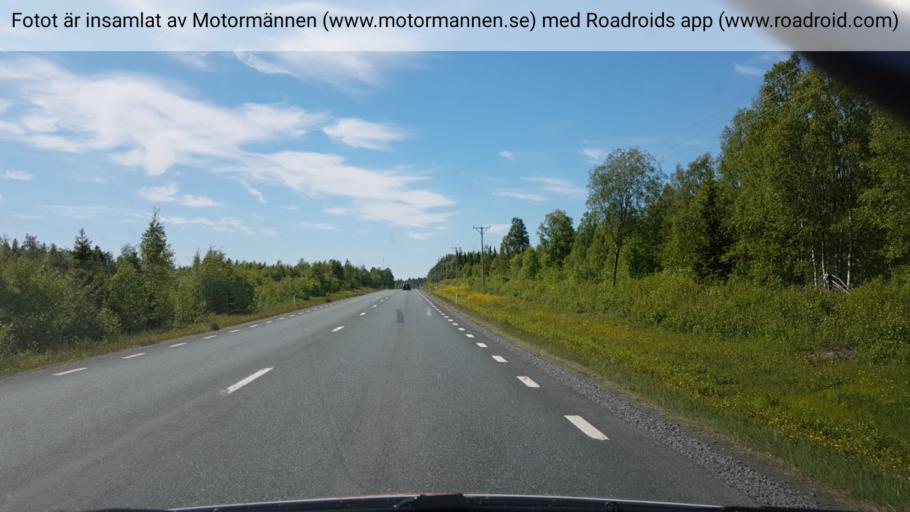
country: SE
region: Norrbotten
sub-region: Haparanda Kommun
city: Haparanda
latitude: 65.8221
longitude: 24.0513
